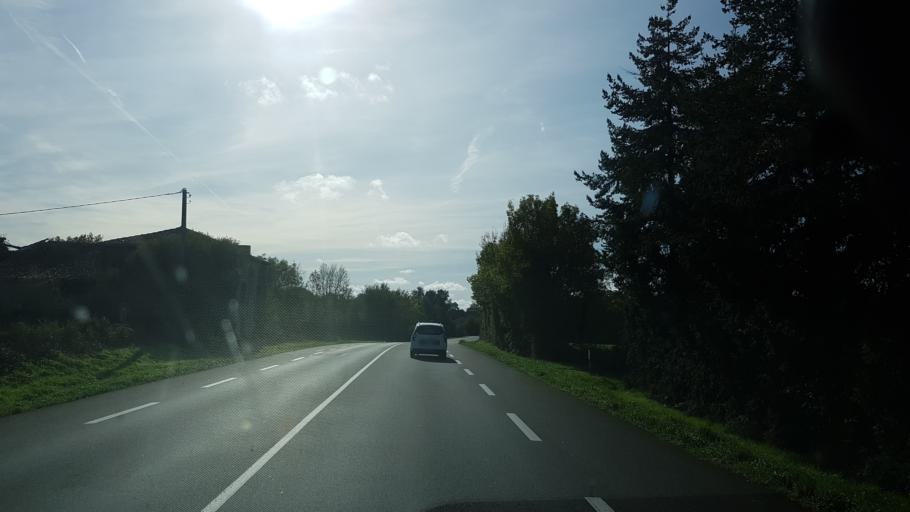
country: FR
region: Poitou-Charentes
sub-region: Departement de la Charente
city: Loubert
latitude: 45.9560
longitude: 0.5734
